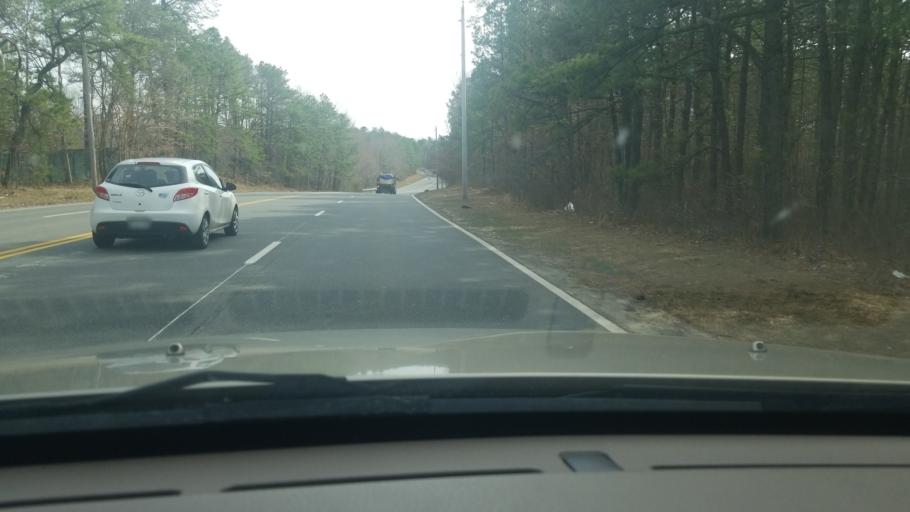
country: US
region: New Jersey
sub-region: Ocean County
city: Vista Center
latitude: 40.1645
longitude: -74.3495
